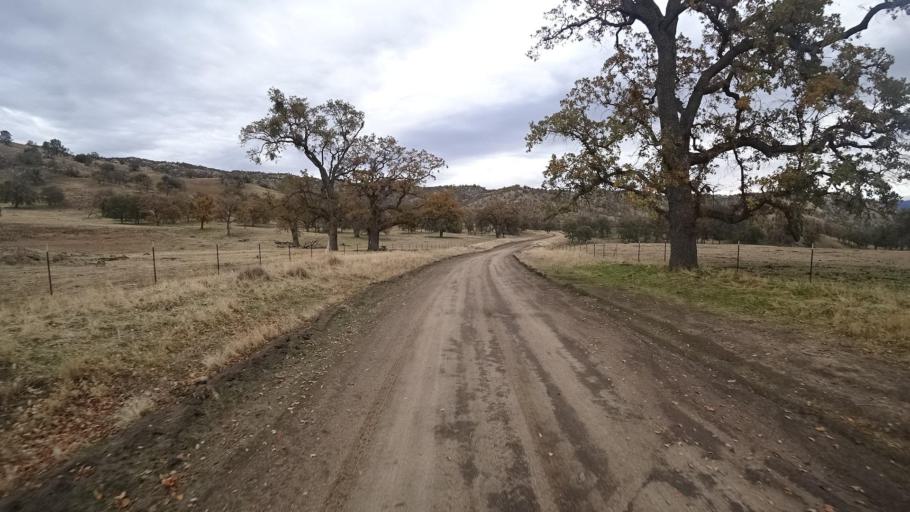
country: US
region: California
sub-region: Kern County
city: Stallion Springs
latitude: 35.1202
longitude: -118.7013
